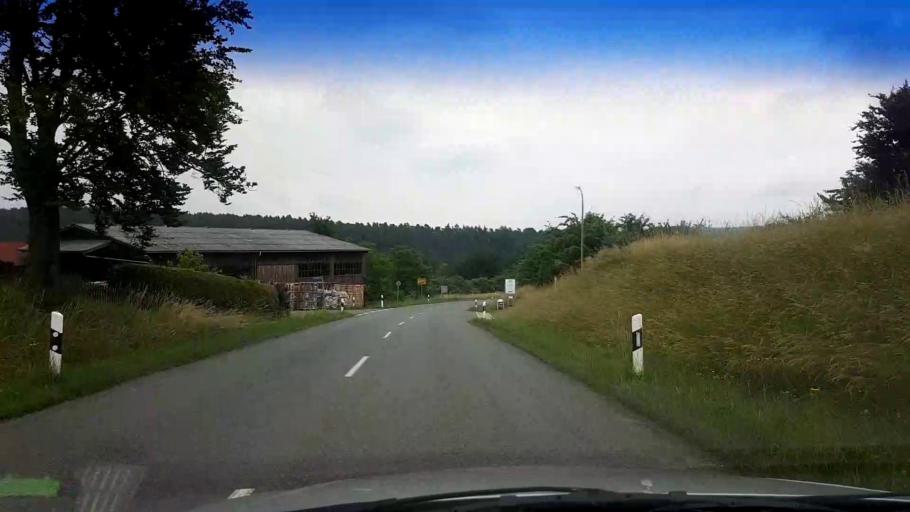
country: DE
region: Bavaria
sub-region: Upper Franconia
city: Kasendorf
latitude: 50.0765
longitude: 11.3245
